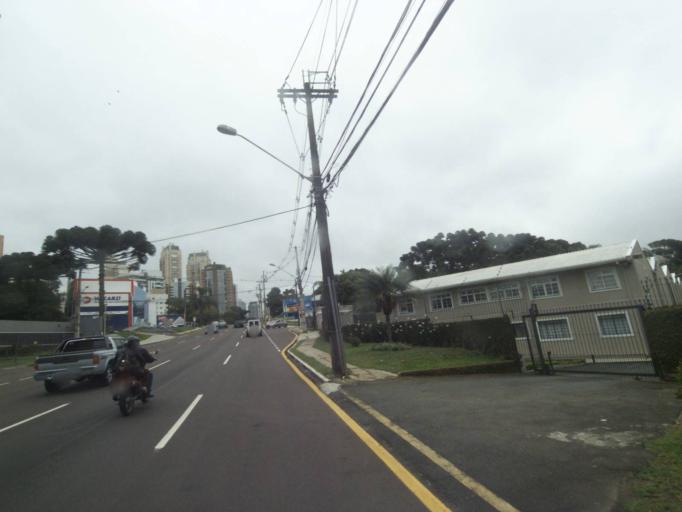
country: BR
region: Parana
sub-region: Curitiba
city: Curitiba
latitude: -25.4357
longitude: -49.3301
